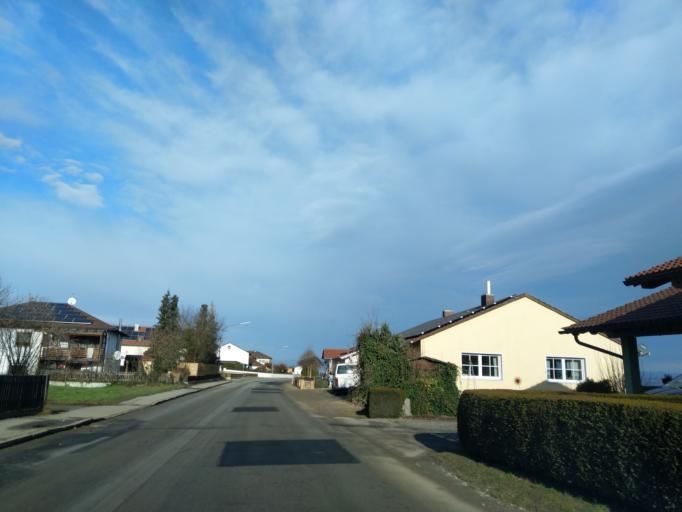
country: DE
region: Bavaria
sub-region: Lower Bavaria
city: Kunzing
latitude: 48.6369
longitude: 13.0284
